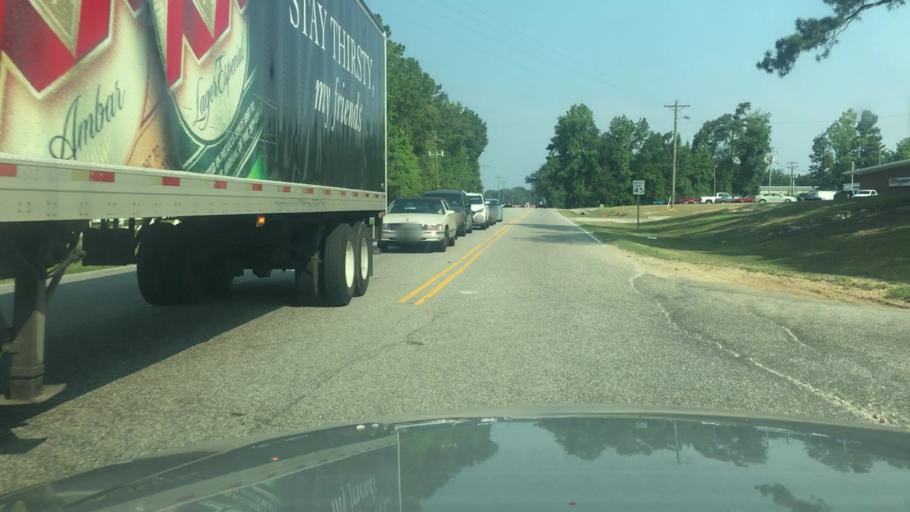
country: US
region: North Carolina
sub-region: Cumberland County
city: Hope Mills
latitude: 34.9297
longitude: -78.9143
